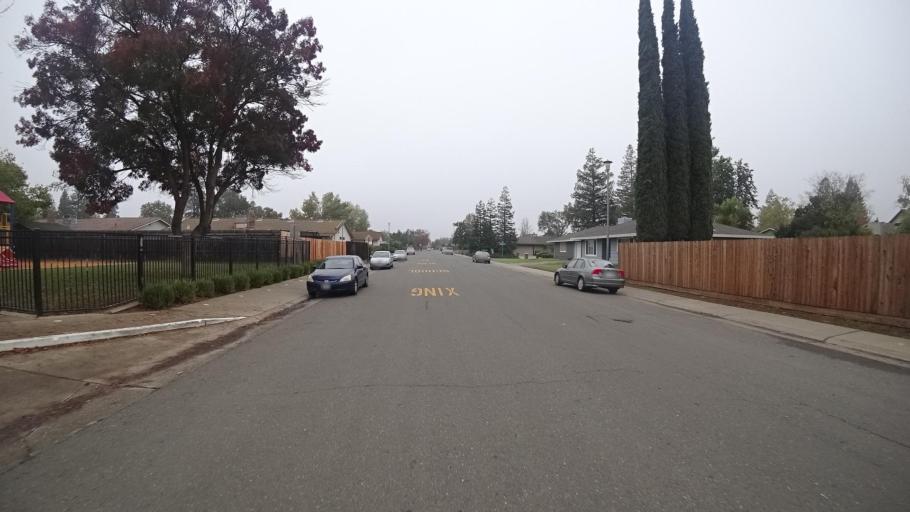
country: US
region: California
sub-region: Sacramento County
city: Elk Grove
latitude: 38.3994
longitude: -121.3692
